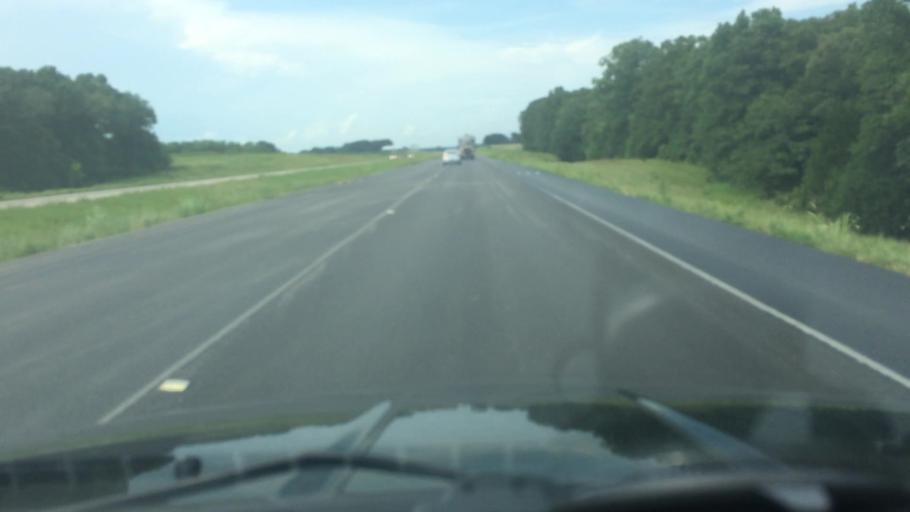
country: US
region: Missouri
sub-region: Saint Clair County
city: Osceola
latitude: 37.9702
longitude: -93.6462
